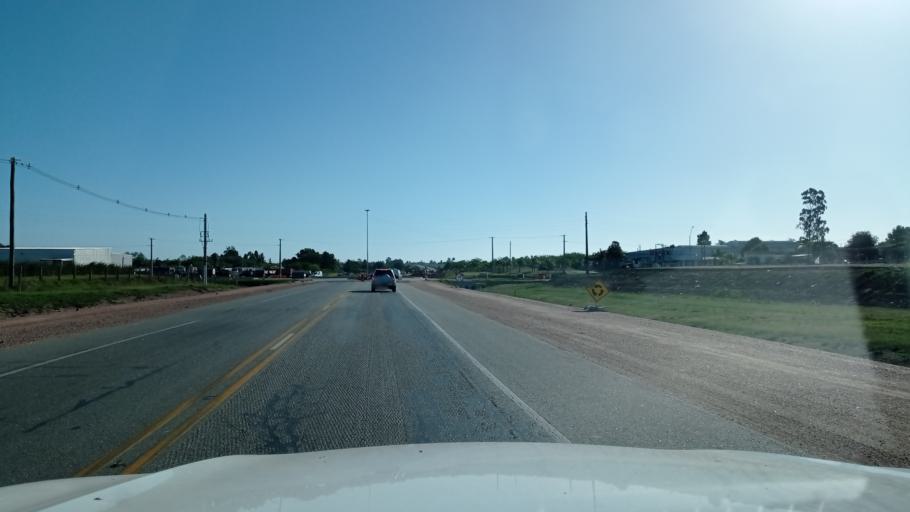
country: UY
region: Canelones
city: Pando
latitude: -34.7278
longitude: -55.9524
